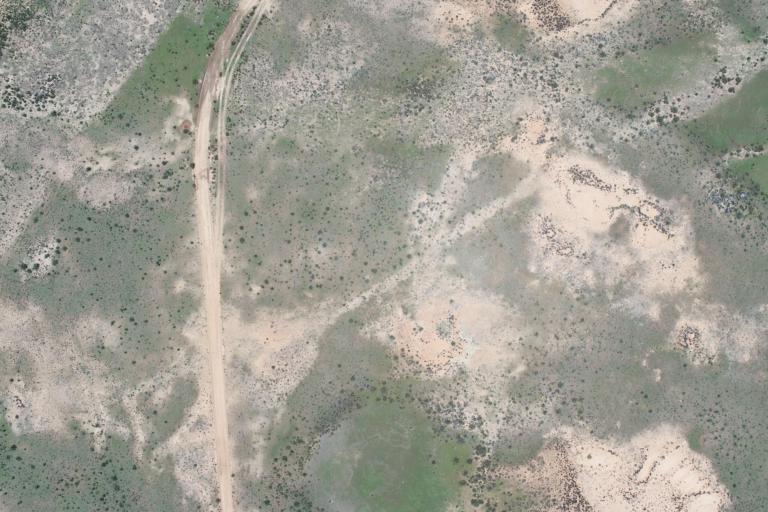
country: BO
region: La Paz
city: Patacamaya
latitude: -17.2828
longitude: -68.5062
